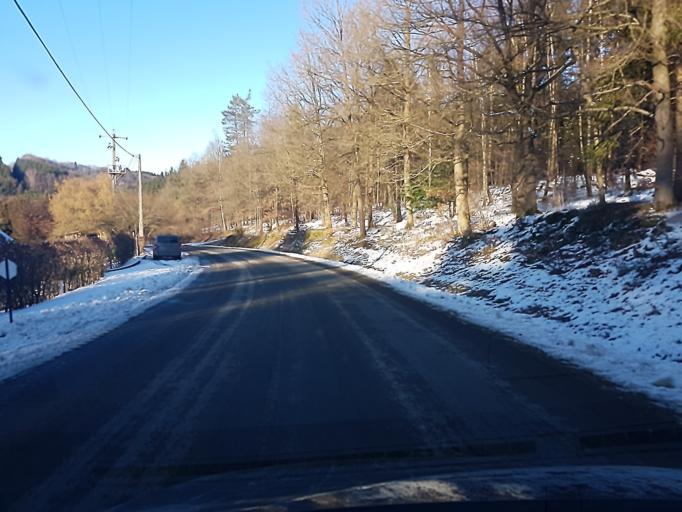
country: BE
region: Wallonia
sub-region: Province de Liege
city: Jalhay
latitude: 50.5414
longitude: 5.9690
